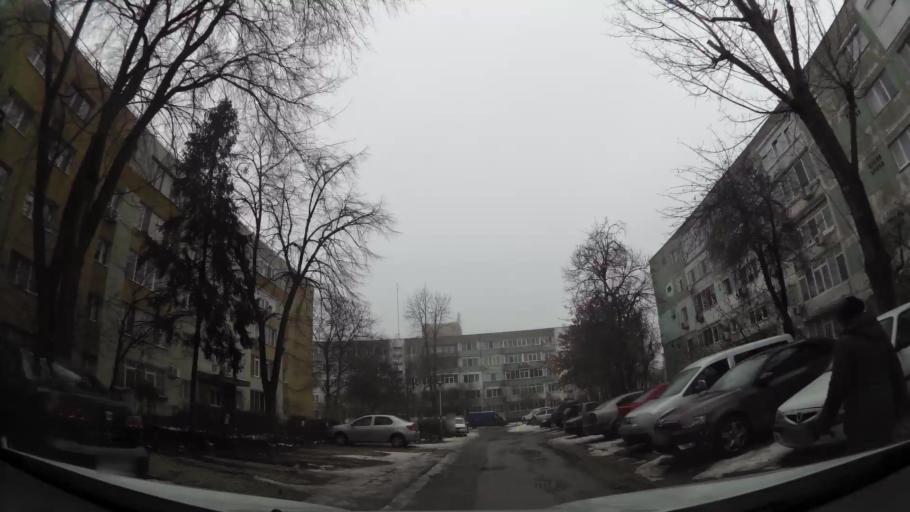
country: RO
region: Ilfov
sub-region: Comuna Chiajna
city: Rosu
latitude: 44.4411
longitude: 26.0146
